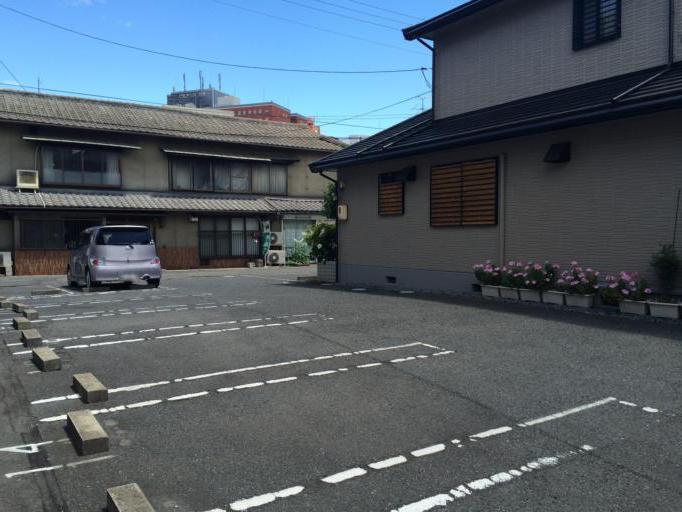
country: JP
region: Okayama
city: Kurashiki
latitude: 34.5991
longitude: 133.7650
